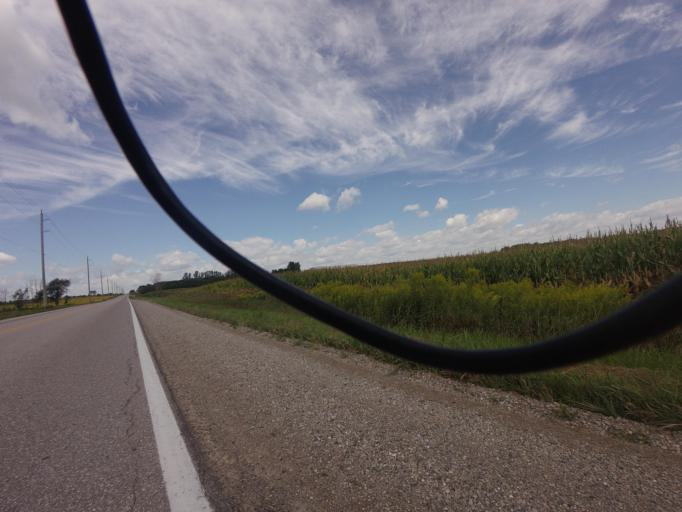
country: CA
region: Ontario
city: Stratford
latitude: 43.4962
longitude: -80.7956
